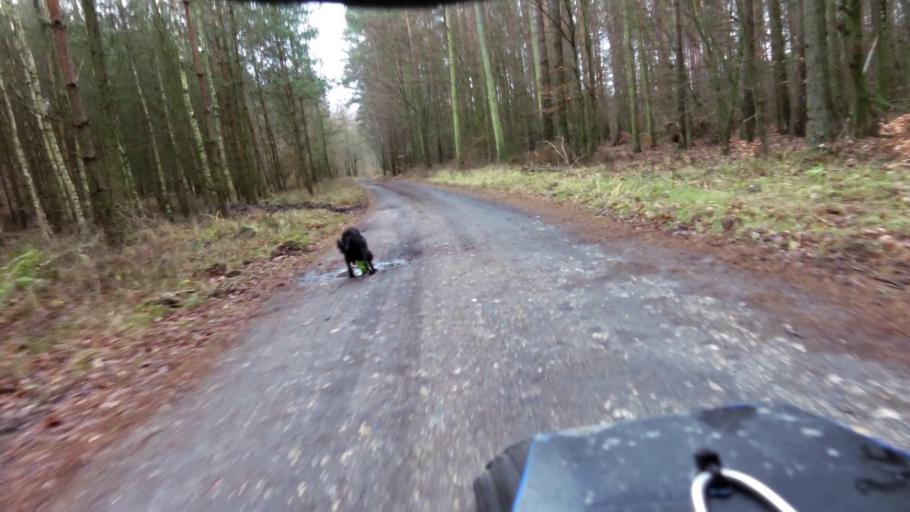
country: PL
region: Lubusz
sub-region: Powiat gorzowski
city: Bogdaniec
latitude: 52.6938
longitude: 15.0337
